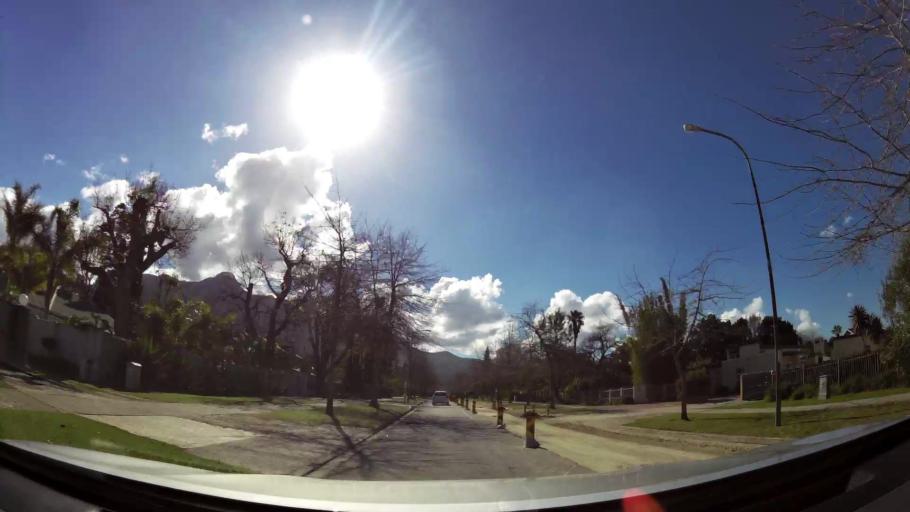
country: ZA
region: Western Cape
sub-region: Eden District Municipality
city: George
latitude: -33.9522
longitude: 22.4607
